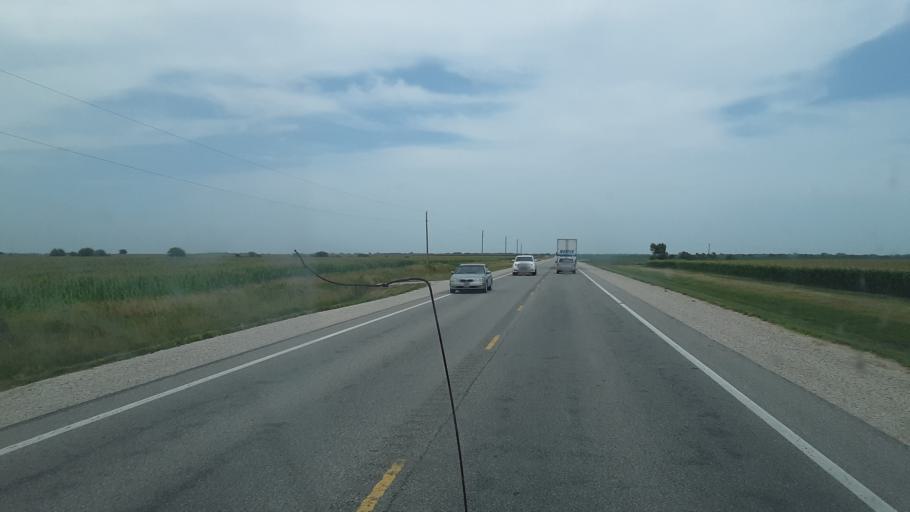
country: US
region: Kansas
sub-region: Allen County
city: Iola
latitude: 37.9218
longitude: -95.2473
